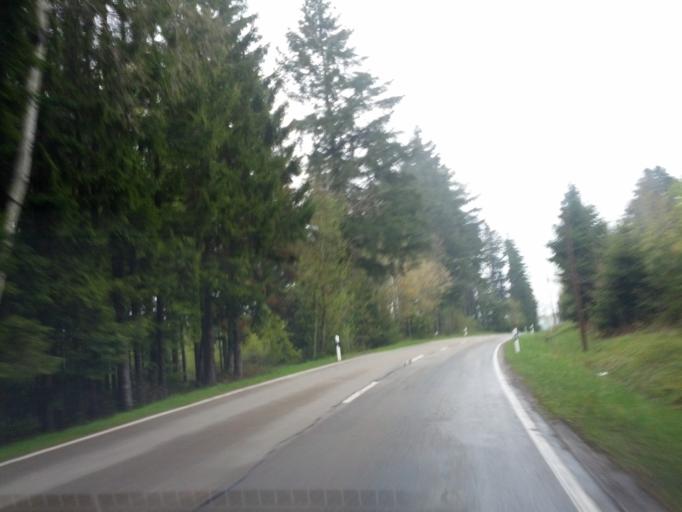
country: DE
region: Baden-Wuerttemberg
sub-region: Freiburg Region
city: Murg
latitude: 47.6015
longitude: 8.0235
